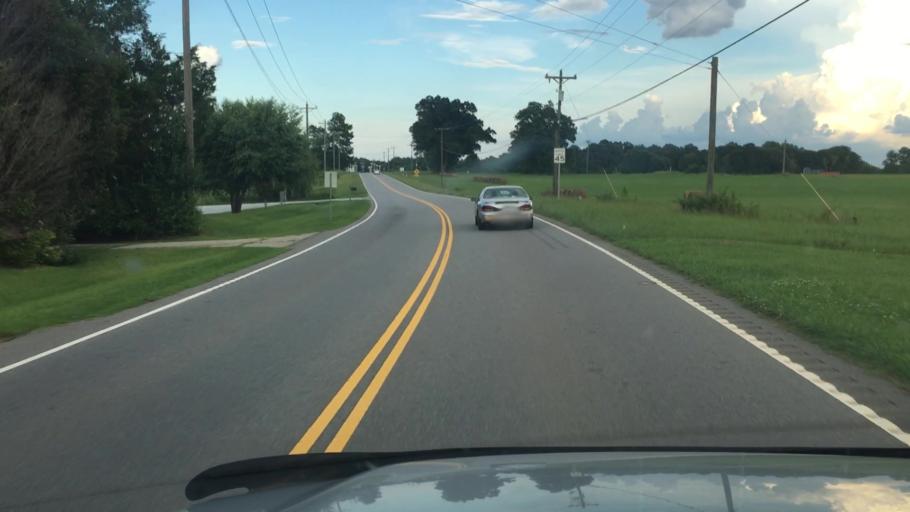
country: US
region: South Carolina
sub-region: Cherokee County
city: Gaffney
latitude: 35.1037
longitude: -81.6907
